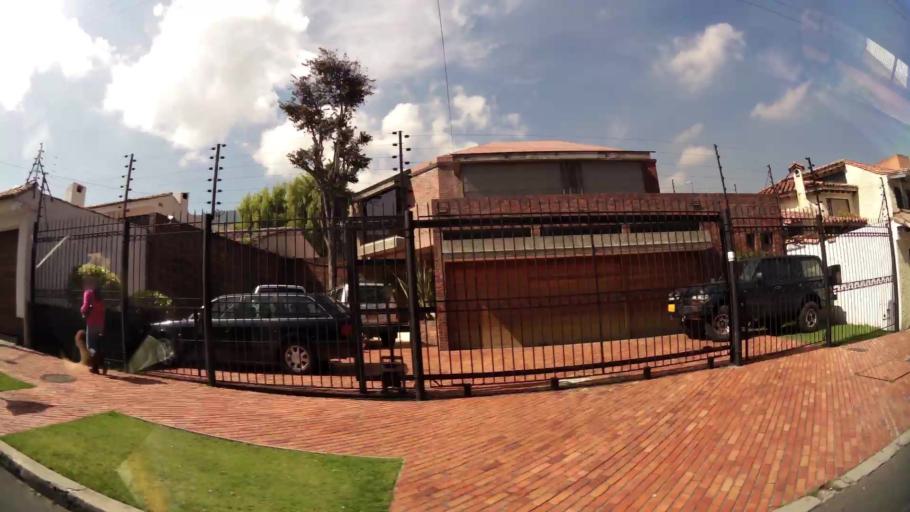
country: CO
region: Bogota D.C.
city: Barrio San Luis
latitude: 4.6901
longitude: -74.0324
